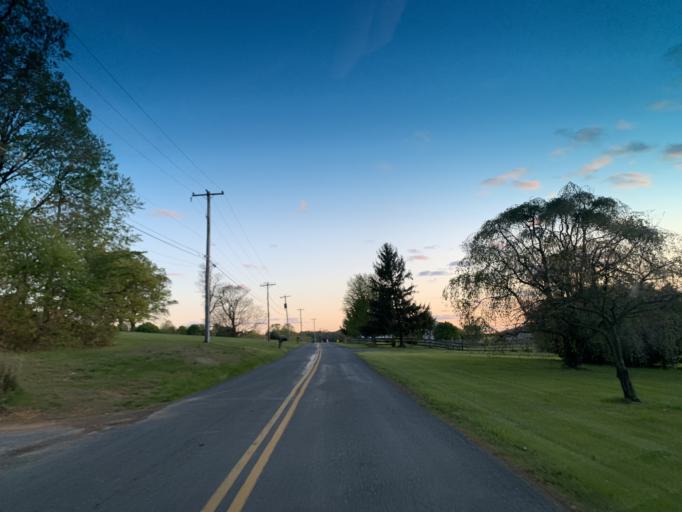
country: US
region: Pennsylvania
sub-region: York County
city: Susquehanna Trails
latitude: 39.6928
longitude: -76.3229
